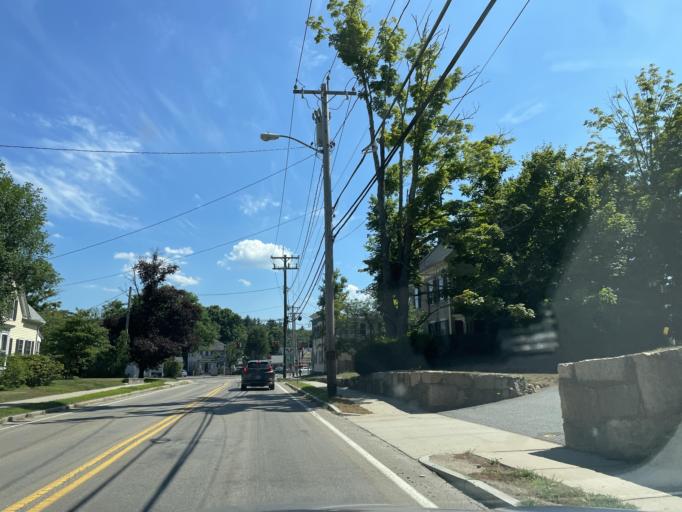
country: US
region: Massachusetts
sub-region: Middlesex County
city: Holliston
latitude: 42.2125
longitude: -71.4255
